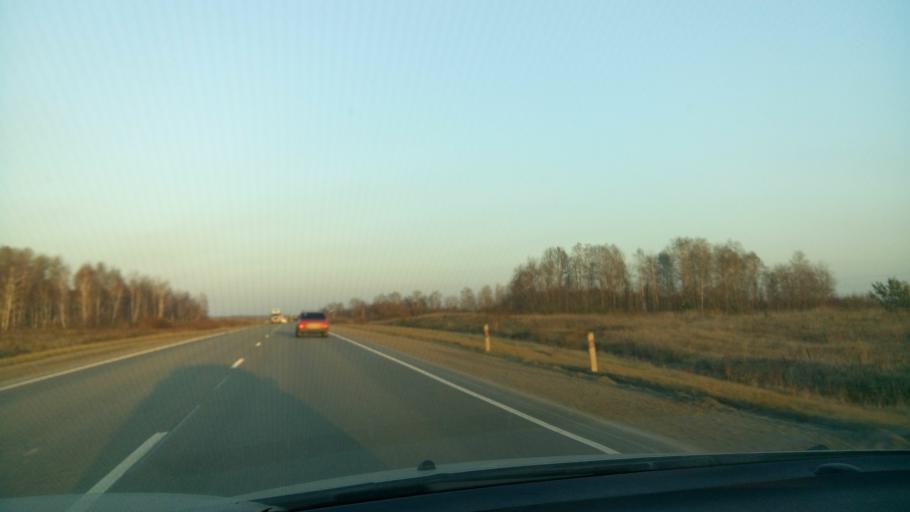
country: RU
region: Sverdlovsk
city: Kamyshlov
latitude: 56.8692
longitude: 62.6719
